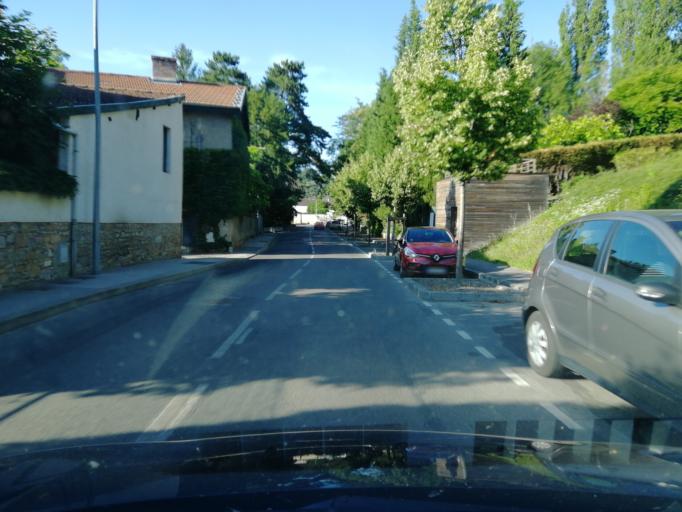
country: FR
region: Rhone-Alpes
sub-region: Departement du Rhone
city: Fontaines-sur-Saone
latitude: 45.8393
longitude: 4.8477
